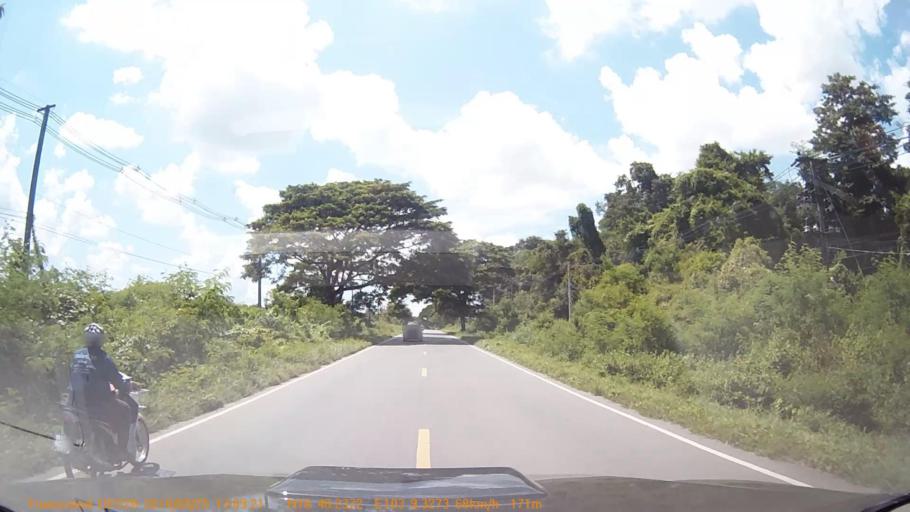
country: TH
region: Khon Kaen
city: Kranuan
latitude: 16.6706
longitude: 103.1555
